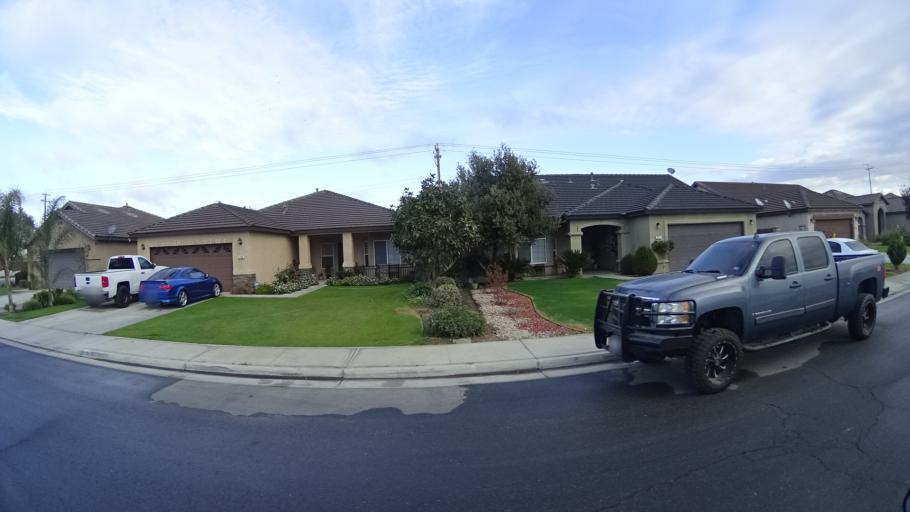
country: US
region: California
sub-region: Kern County
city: Greenfield
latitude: 35.2880
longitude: -118.9981
